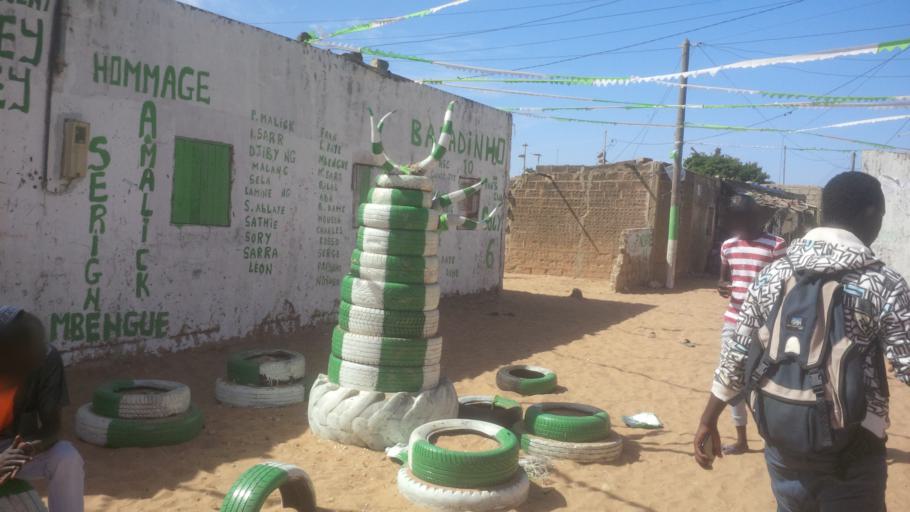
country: SN
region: Dakar
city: Pikine
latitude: 14.7739
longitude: -17.3755
